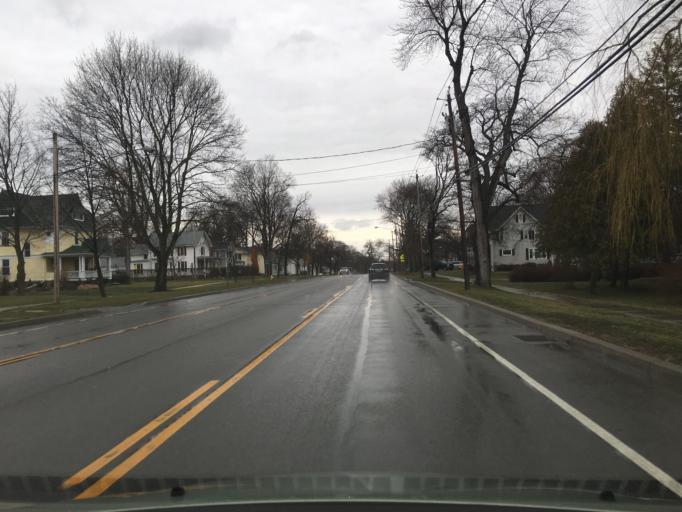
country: US
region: New York
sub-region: Livingston County
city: Avon
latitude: 42.9108
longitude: -77.7386
